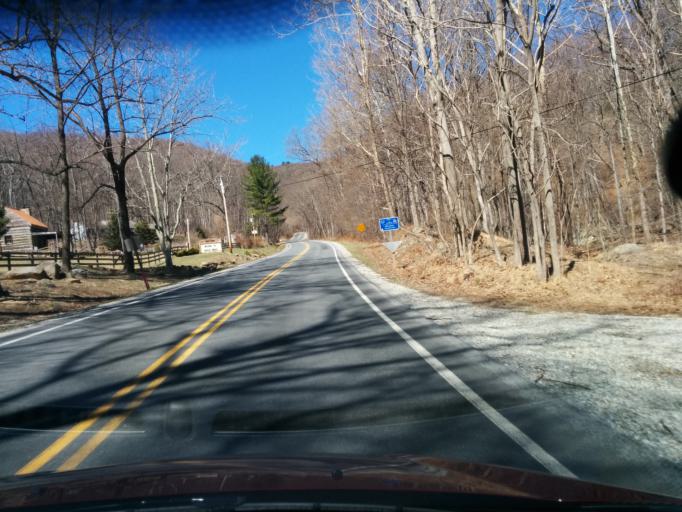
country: US
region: Virginia
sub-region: Nelson County
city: Nellysford
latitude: 37.8902
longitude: -78.9732
